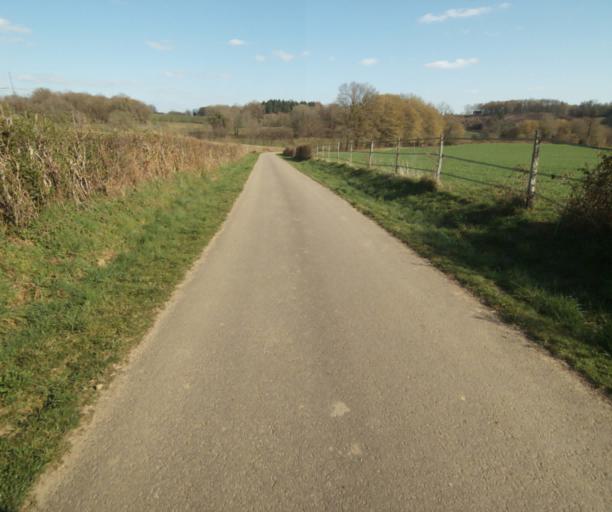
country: FR
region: Limousin
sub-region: Departement de la Correze
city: Saint-Mexant
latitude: 45.3251
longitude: 1.6152
